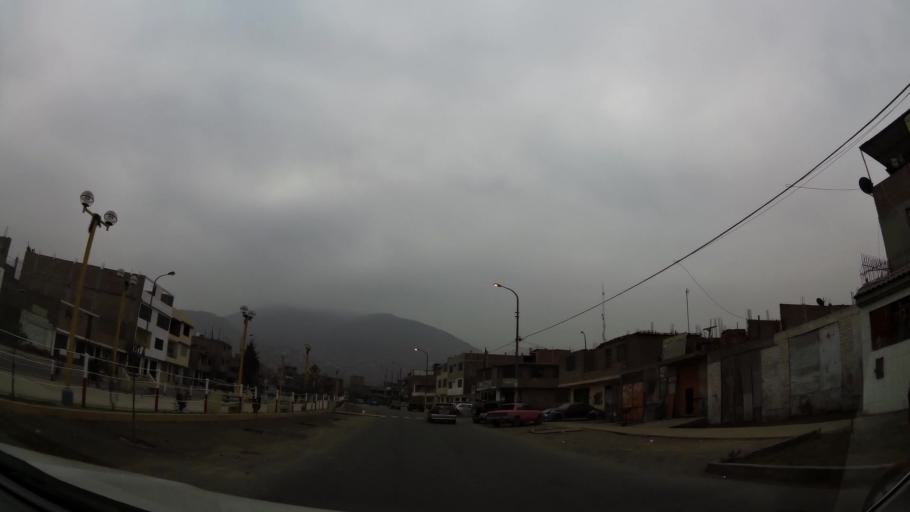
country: PE
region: Lima
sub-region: Lima
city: Independencia
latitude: -11.9637
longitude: -76.9996
